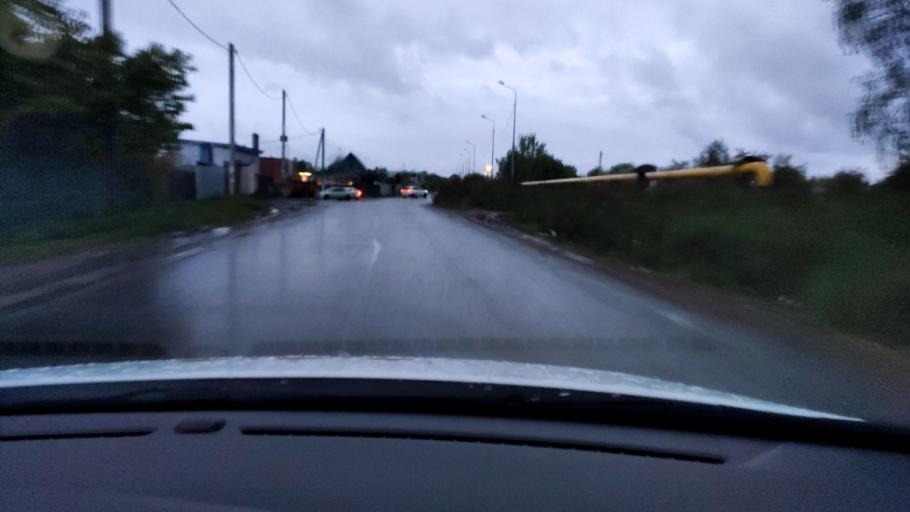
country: RU
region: Tatarstan
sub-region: Gorod Kazan'
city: Kazan
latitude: 55.7237
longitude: 49.1105
